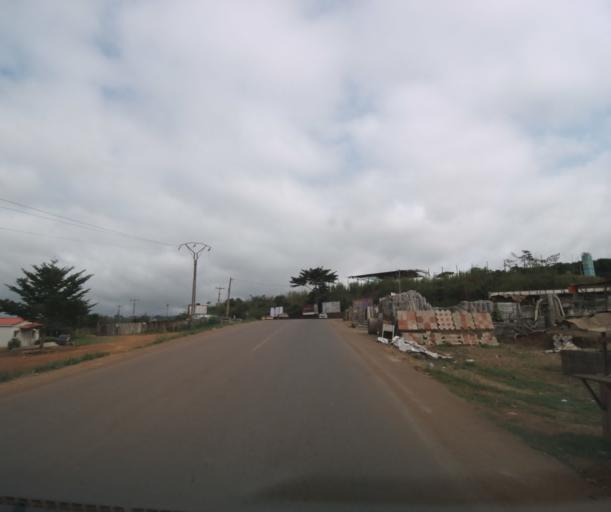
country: CM
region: Centre
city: Yaounde
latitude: 3.8069
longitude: 11.5192
